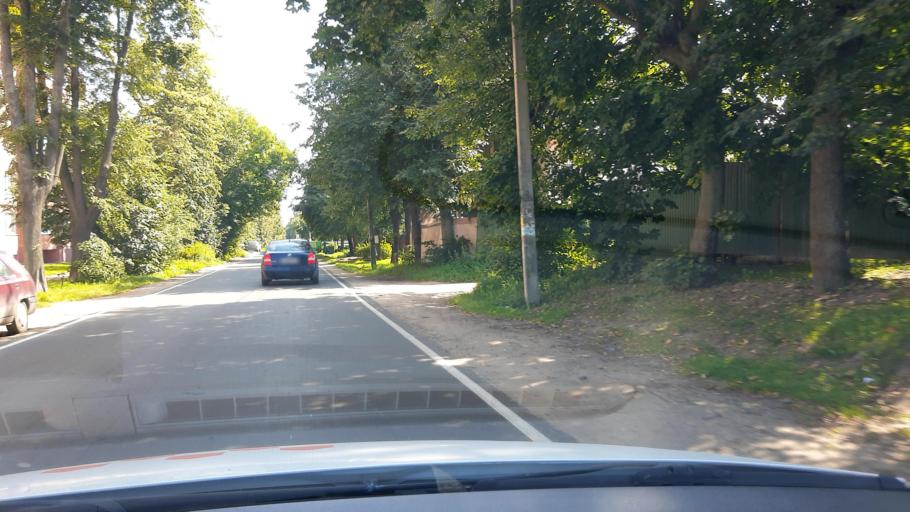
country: RU
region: Moskovskaya
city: Bronnitsy
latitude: 55.4229
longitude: 38.2629
